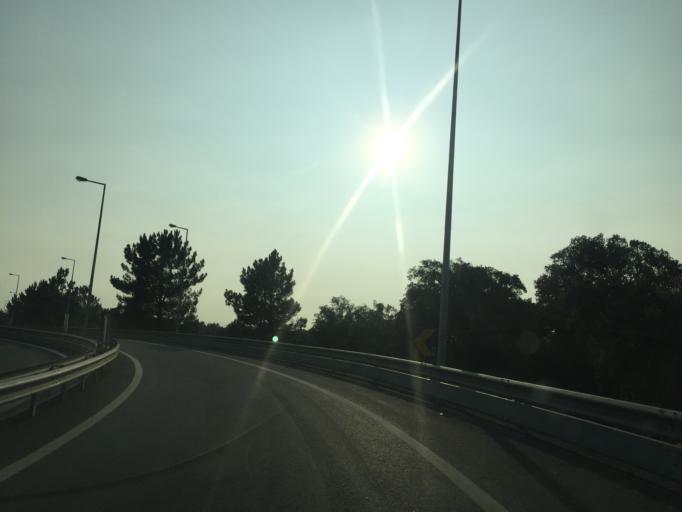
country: PT
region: Setubal
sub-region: Setubal
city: Setubal
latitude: 38.6023
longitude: -8.6748
